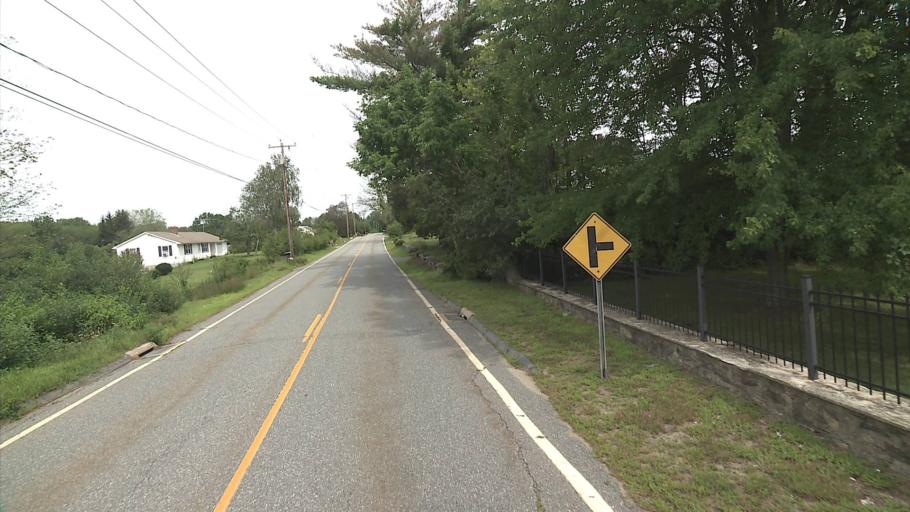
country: US
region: Connecticut
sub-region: Windham County
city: Thompson
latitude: 41.9963
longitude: -71.8447
